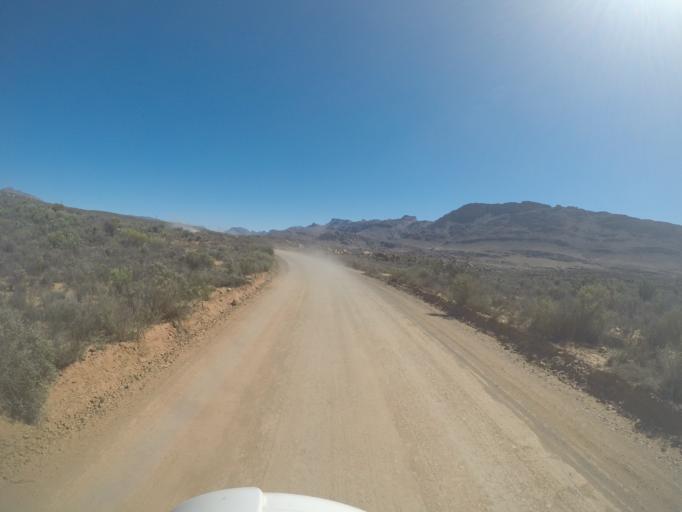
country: ZA
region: Western Cape
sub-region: West Coast District Municipality
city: Clanwilliam
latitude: -32.5015
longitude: 19.2795
